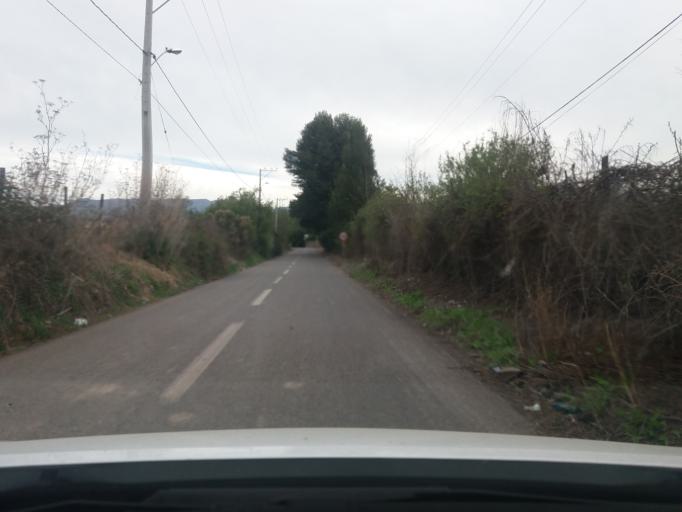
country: CL
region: Valparaiso
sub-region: Provincia de Los Andes
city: Los Andes
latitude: -32.8489
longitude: -70.6297
